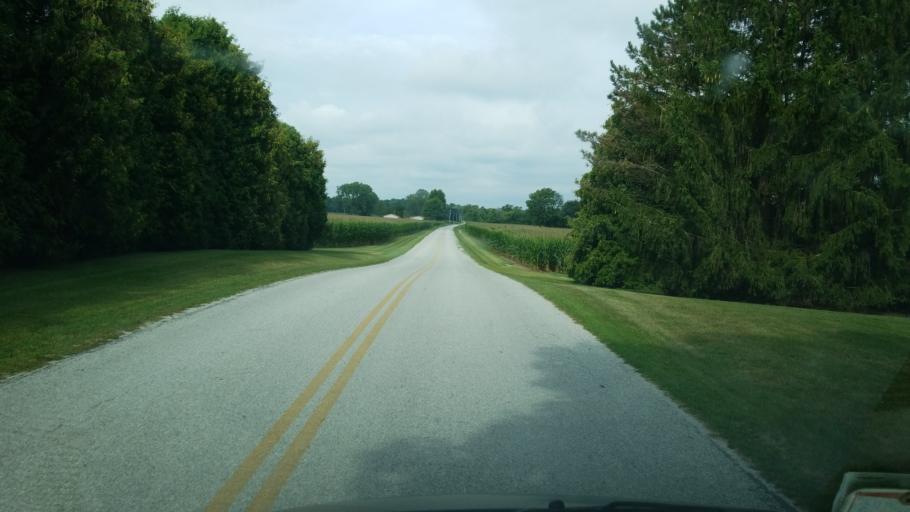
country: US
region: Ohio
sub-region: Sandusky County
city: Green Springs
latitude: 41.1895
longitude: -83.1089
